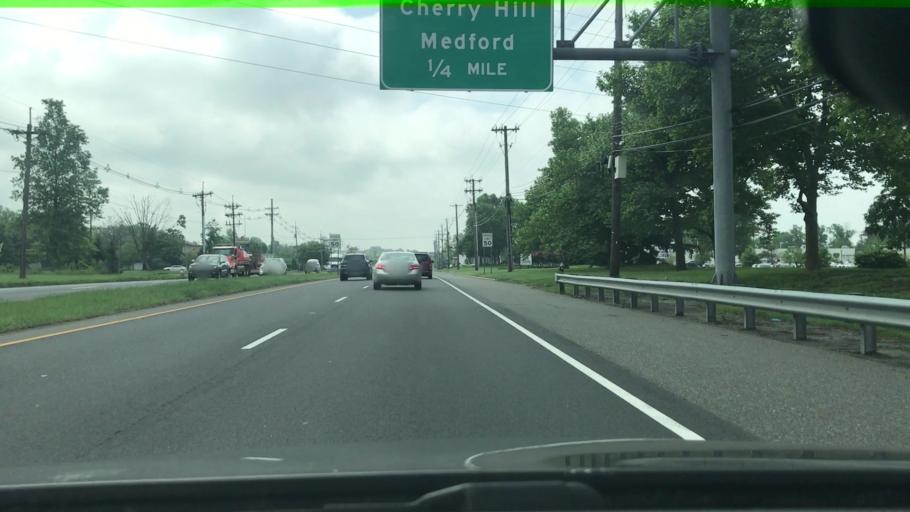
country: US
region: New Jersey
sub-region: Burlington County
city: Marlton
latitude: 39.9007
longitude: -74.9334
